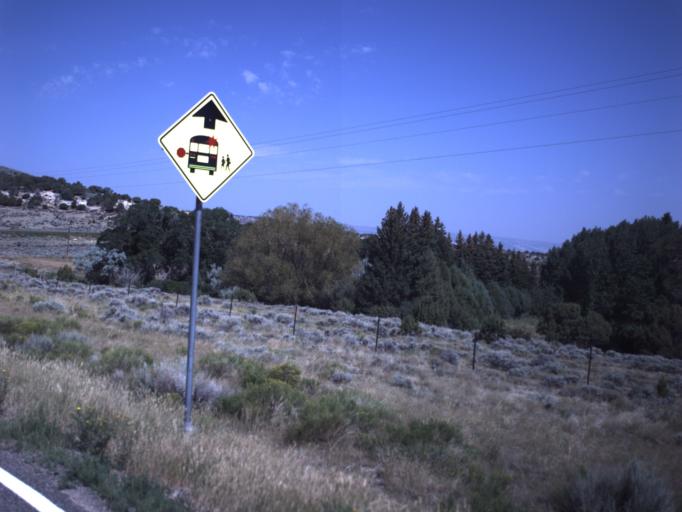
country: US
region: Utah
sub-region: Daggett County
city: Manila
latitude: 40.9781
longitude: -109.8340
